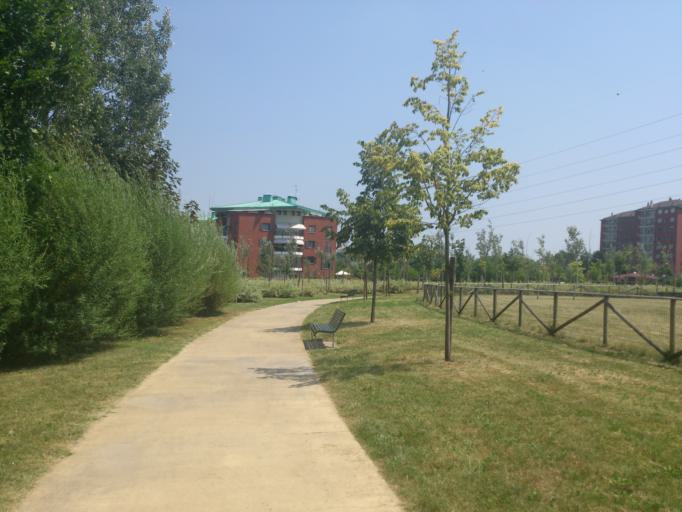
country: IT
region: Lombardy
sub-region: Citta metropolitana di Milano
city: Cologno Monzese
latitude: 45.5181
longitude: 9.2754
